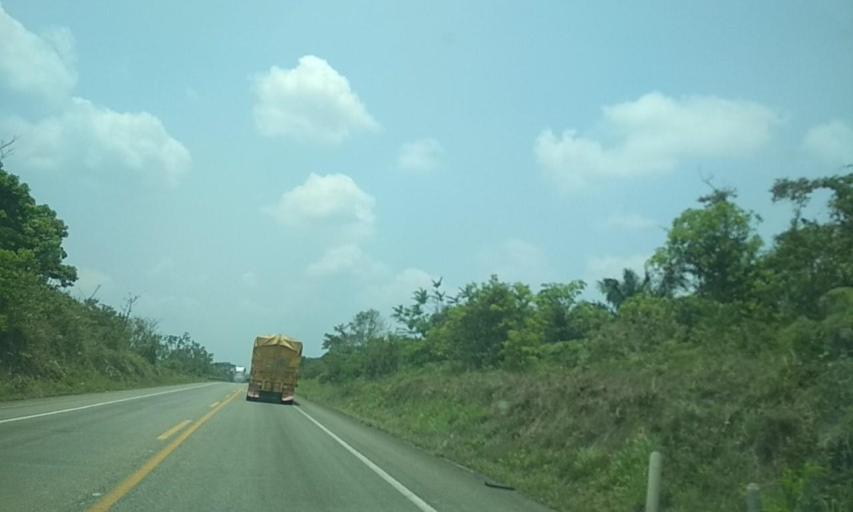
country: MX
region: Tabasco
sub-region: Huimanguillo
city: Francisco Rueda
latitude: 17.7311
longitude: -93.9683
